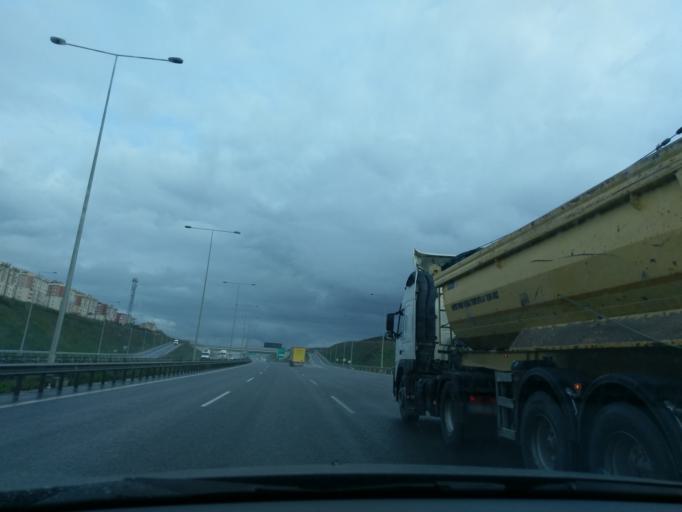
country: TR
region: Istanbul
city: Basaksehir
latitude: 41.0887
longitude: 28.8138
